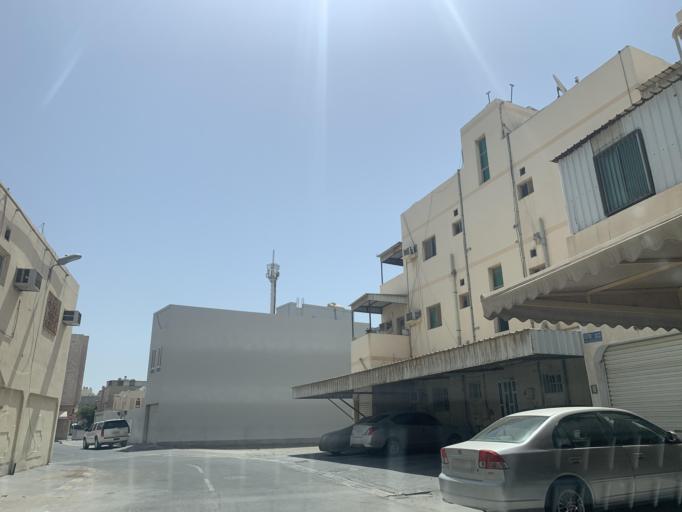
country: BH
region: Northern
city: Sitrah
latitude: 26.1584
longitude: 50.6141
